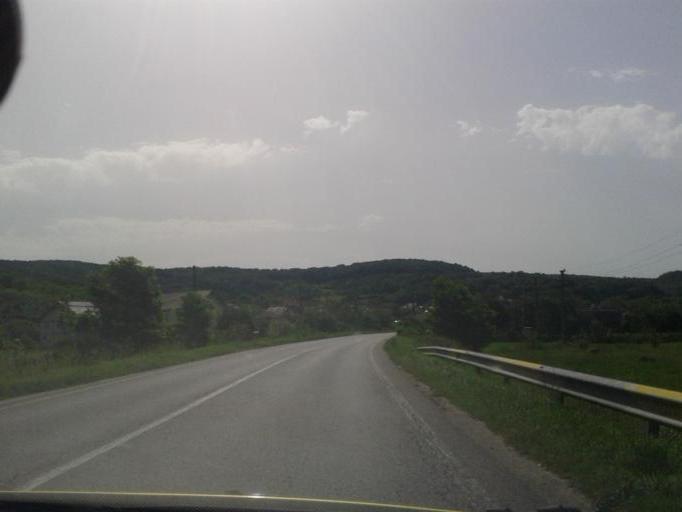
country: RO
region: Valcea
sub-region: Comuna Mihaesti
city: Mihaesti
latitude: 45.0621
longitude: 24.2435
